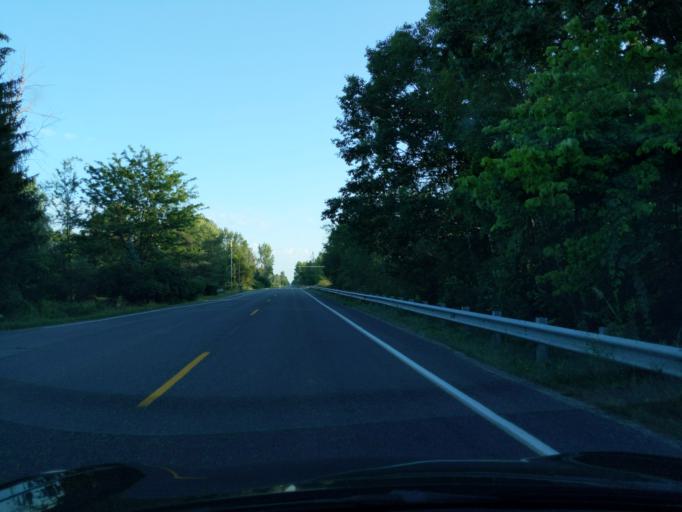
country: US
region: Michigan
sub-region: Midland County
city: Midland
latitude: 43.5545
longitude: -84.3697
